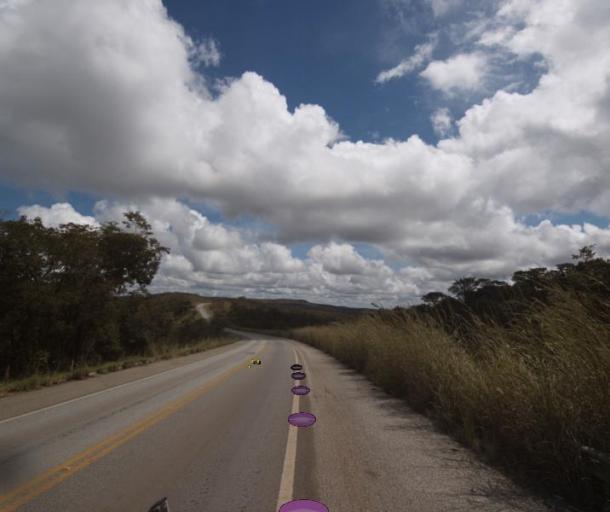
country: BR
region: Goias
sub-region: Pirenopolis
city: Pirenopolis
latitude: -15.7706
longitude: -48.5481
